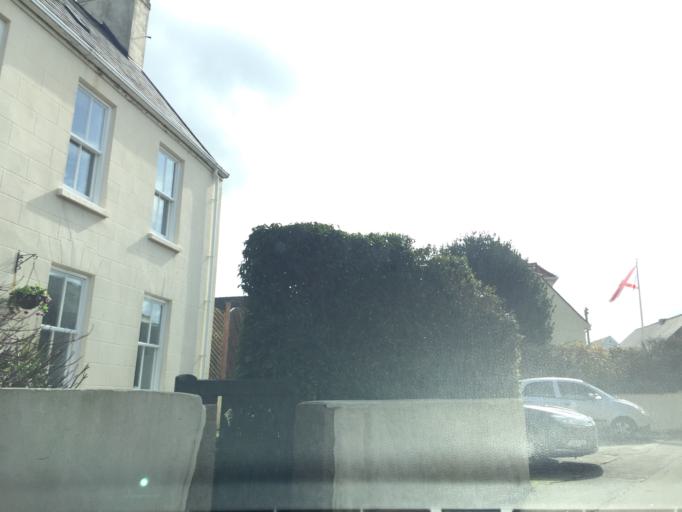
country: JE
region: St Helier
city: Saint Helier
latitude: 49.2044
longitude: -2.0714
